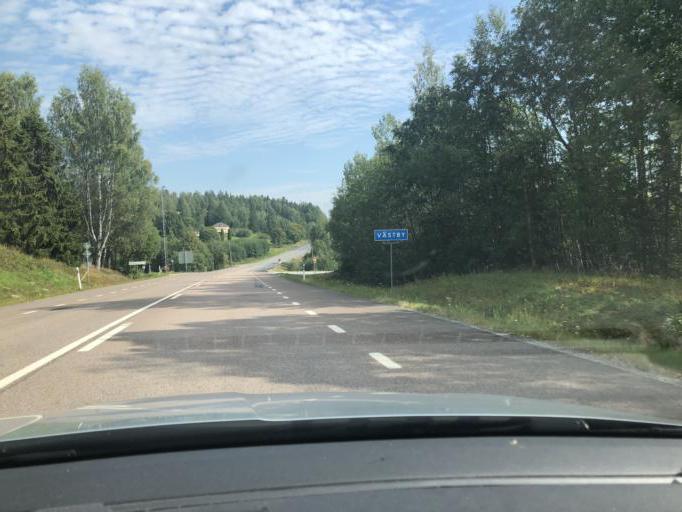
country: SE
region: Vaesternorrland
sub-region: Kramfors Kommun
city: Kramfors
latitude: 62.8291
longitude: 17.8552
